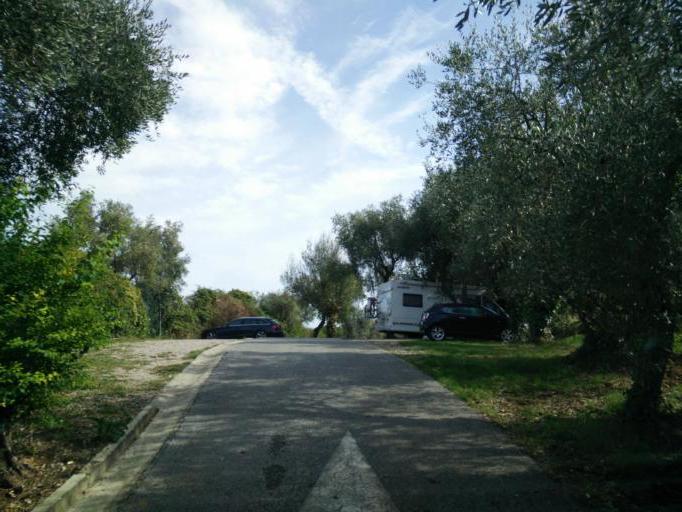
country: IT
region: Liguria
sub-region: Provincia di La Spezia
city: Le Grazie
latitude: 44.0604
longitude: 9.8453
